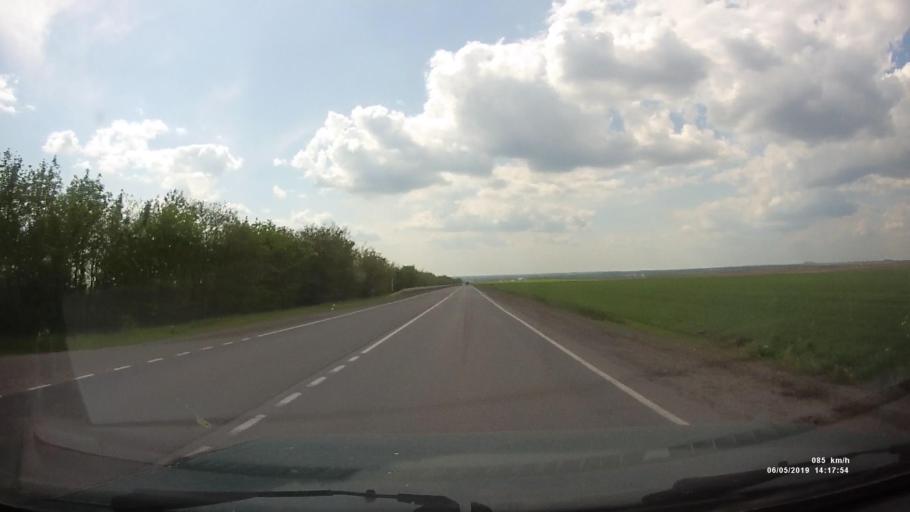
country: RU
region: Rostov
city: Kamenolomni
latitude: 47.6338
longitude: 40.2599
